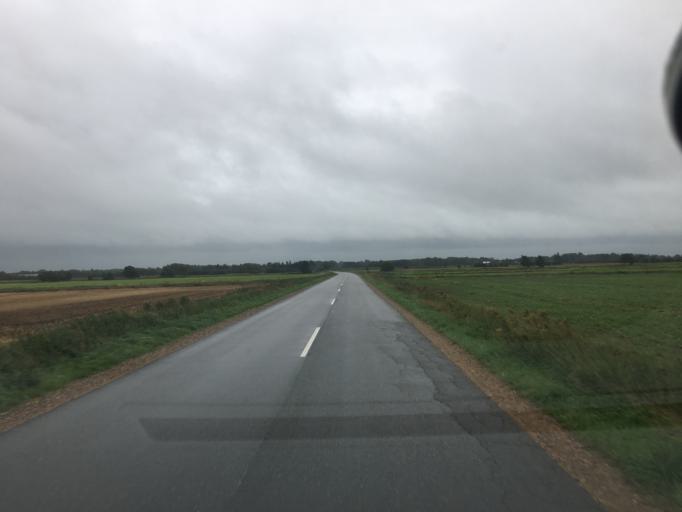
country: DE
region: Schleswig-Holstein
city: Bramstedtlund
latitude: 54.9705
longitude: 9.0449
